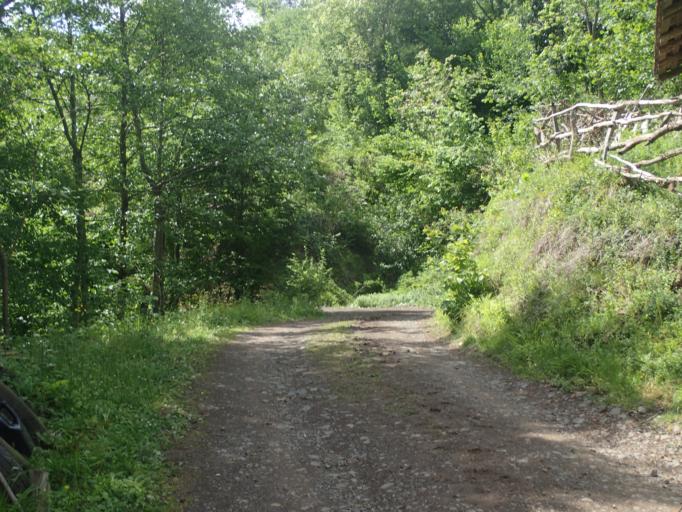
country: TR
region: Ordu
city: Akkus
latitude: 40.9057
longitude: 36.8824
